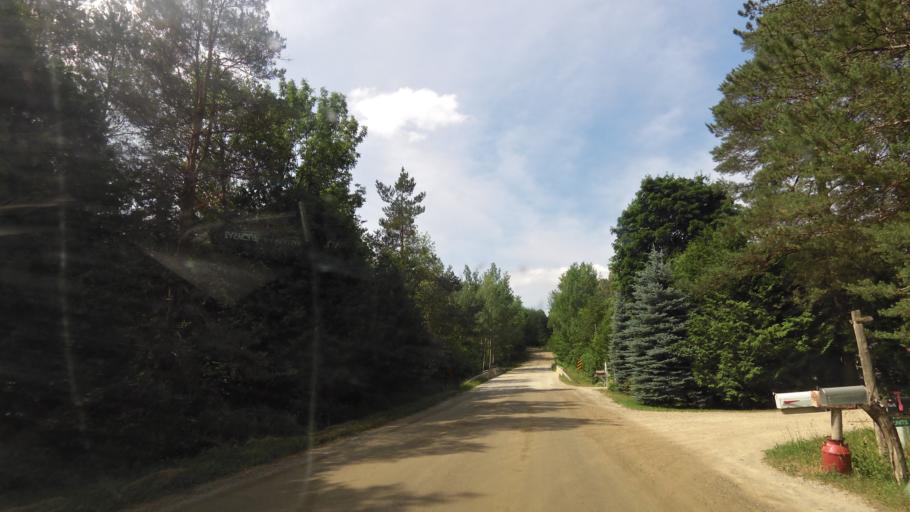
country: CA
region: Ontario
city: Orangeville
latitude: 43.9877
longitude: -80.0465
